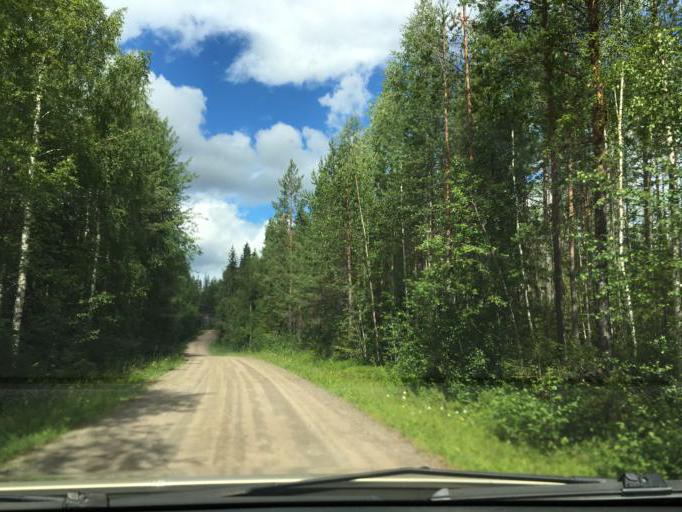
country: SE
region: Norrbotten
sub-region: Overkalix Kommun
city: OEverkalix
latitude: 66.1319
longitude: 22.7846
